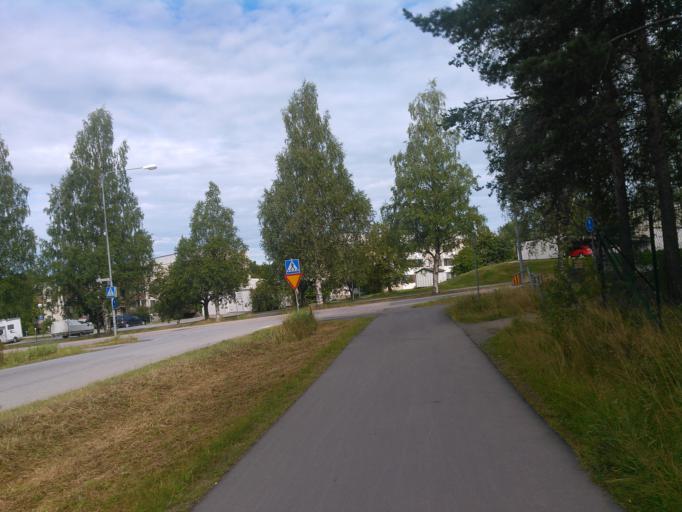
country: SE
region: Vaesterbotten
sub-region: Umea Kommun
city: Ersmark
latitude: 63.8313
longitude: 20.3225
